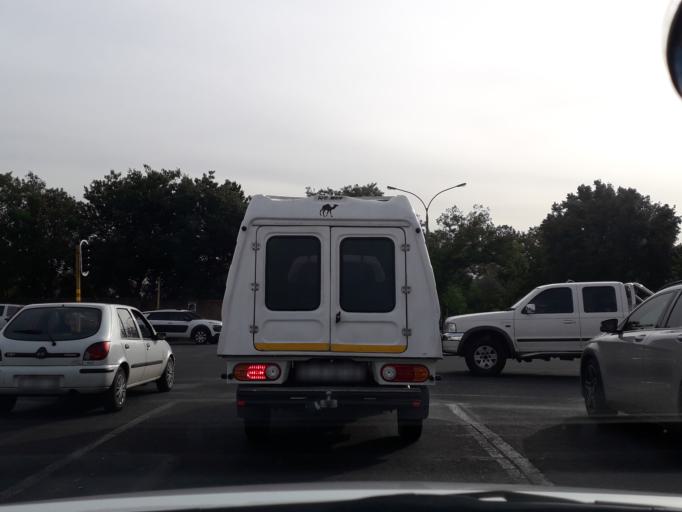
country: ZA
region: Gauteng
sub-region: City of Johannesburg Metropolitan Municipality
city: Modderfontein
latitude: -26.1533
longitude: 28.1528
